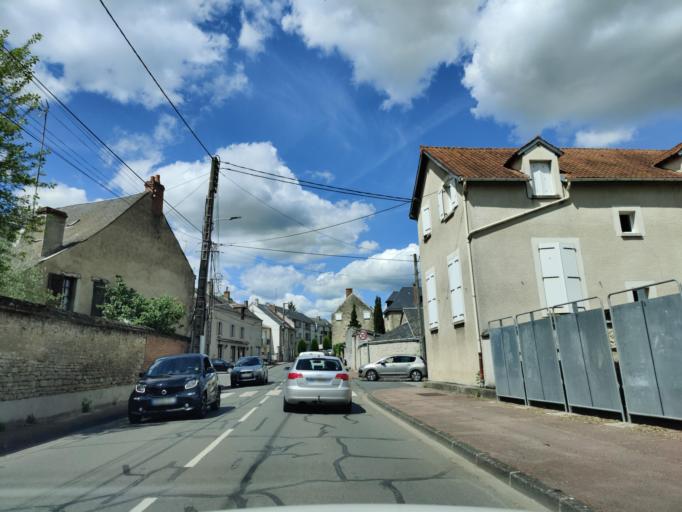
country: FR
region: Centre
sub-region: Departement du Loiret
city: Pithiviers
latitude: 48.1669
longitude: 2.2562
